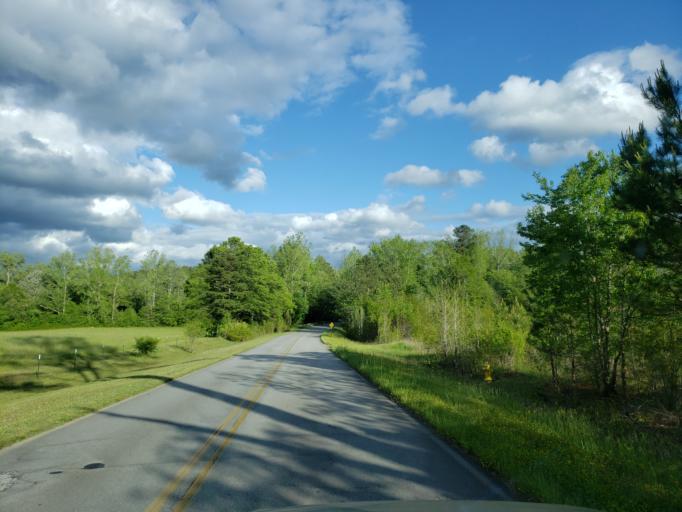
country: US
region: Georgia
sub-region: Haralson County
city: Tallapoosa
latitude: 33.7788
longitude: -85.3120
